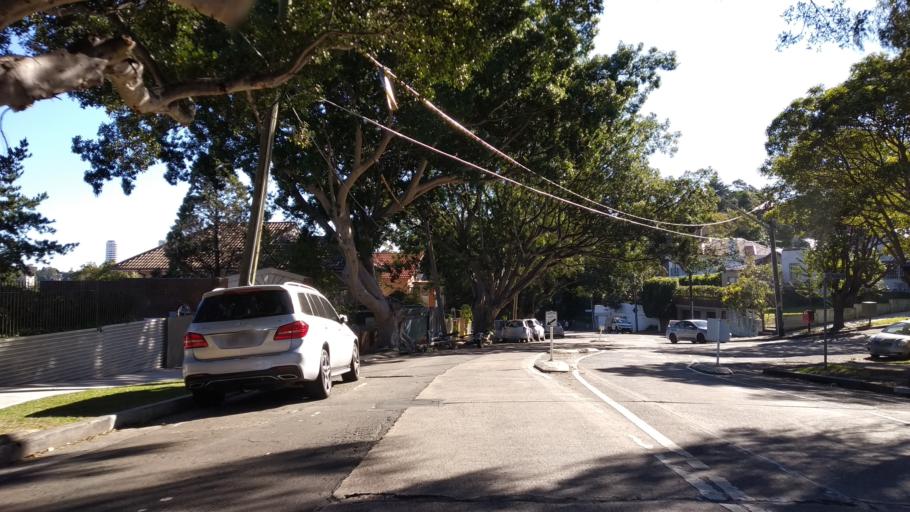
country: AU
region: New South Wales
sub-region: Woollahra
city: Bellevue Hill
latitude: -33.8802
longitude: 151.2486
